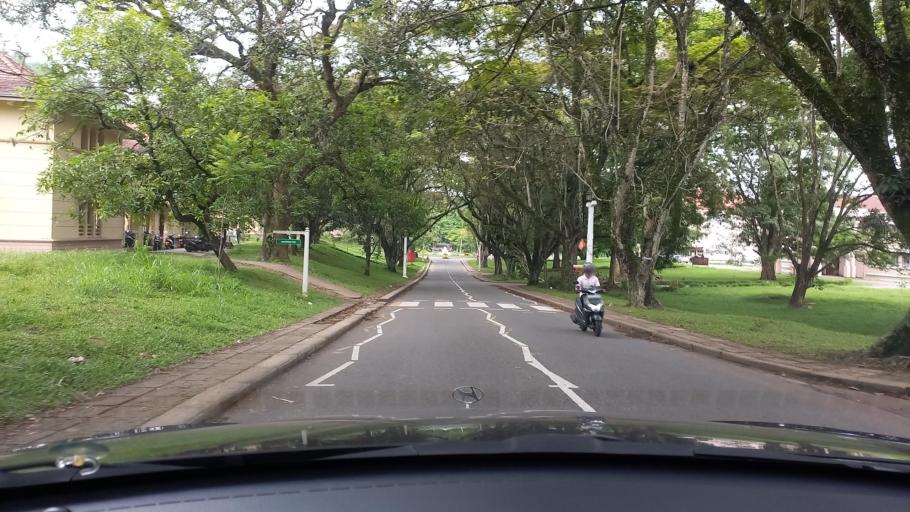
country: LK
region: Central
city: Kandy
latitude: 7.2603
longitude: 80.5997
